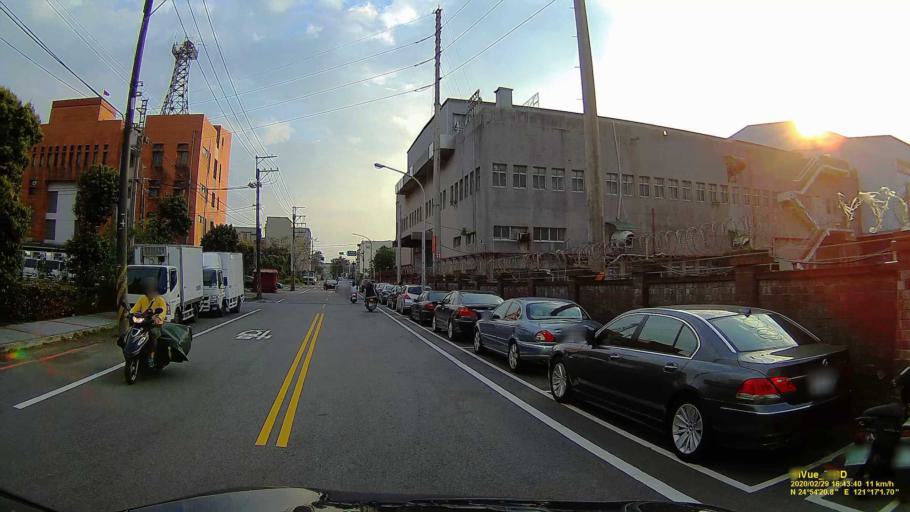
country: TW
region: Taiwan
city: Daxi
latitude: 24.9057
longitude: 121.2838
